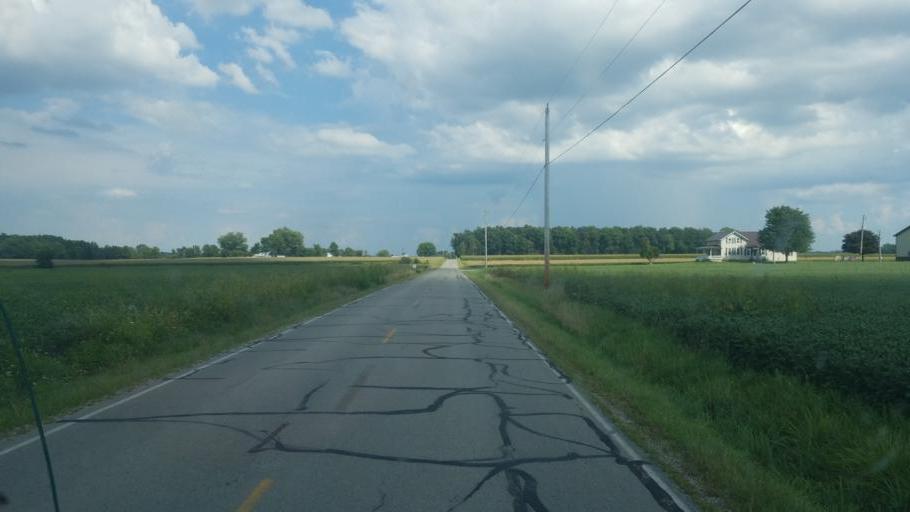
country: US
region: Ohio
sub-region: Huron County
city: Willard
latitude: 40.9819
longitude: -82.8100
